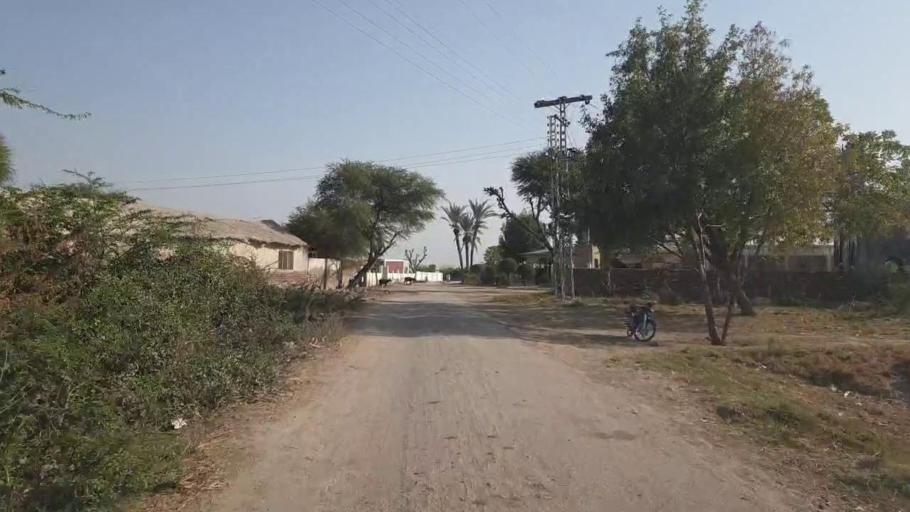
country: PK
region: Sindh
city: Dhoro Naro
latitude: 25.4645
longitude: 69.5512
